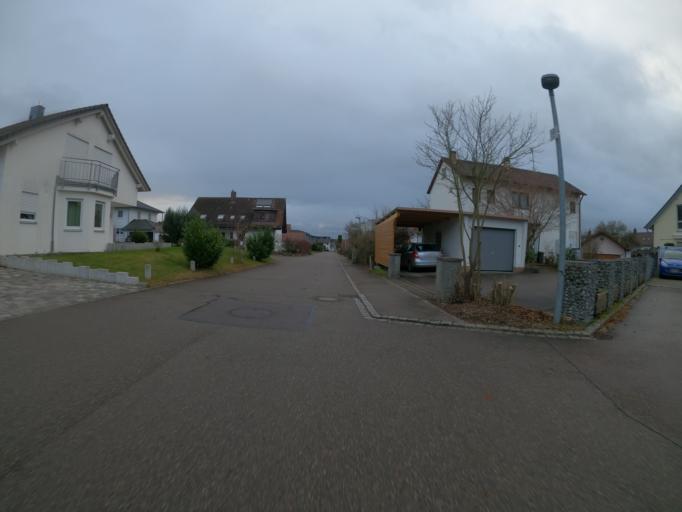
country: DE
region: Baden-Wuerttemberg
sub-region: Regierungsbezirk Stuttgart
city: Waschenbeuren
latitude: 48.7637
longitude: 9.6913
